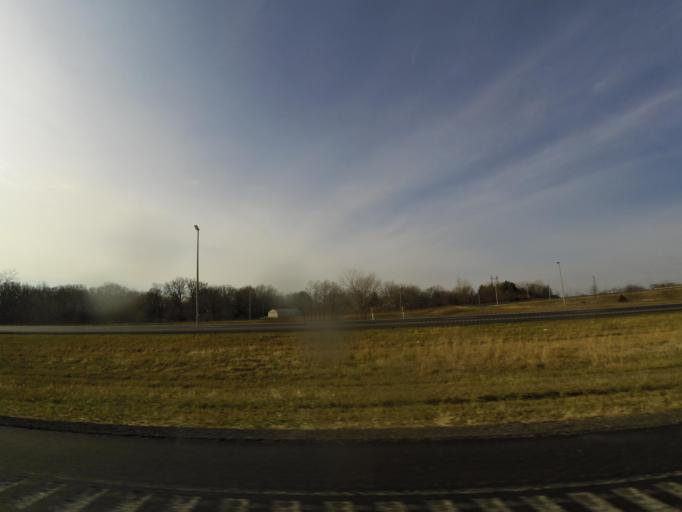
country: US
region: Illinois
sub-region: Macon County
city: Harristown
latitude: 39.8359
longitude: -89.0444
